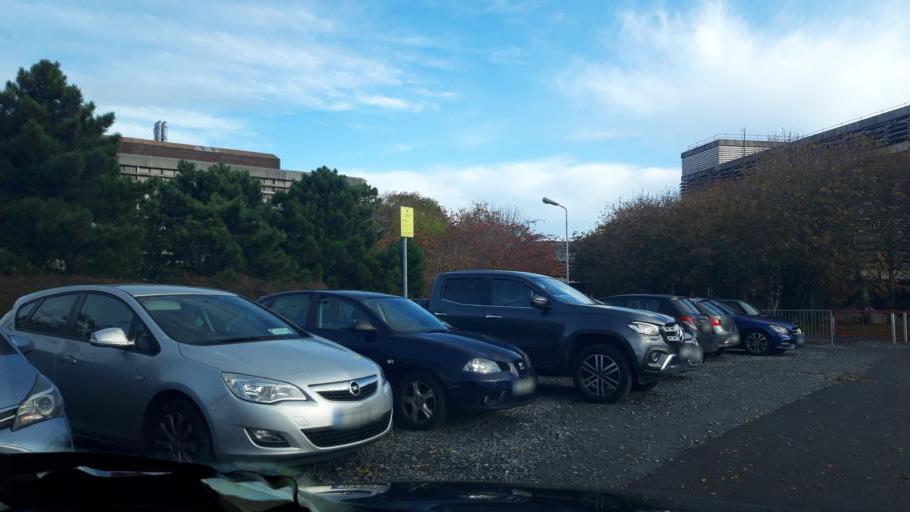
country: IE
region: Leinster
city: Donnybrook
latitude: 53.3063
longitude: -6.2250
